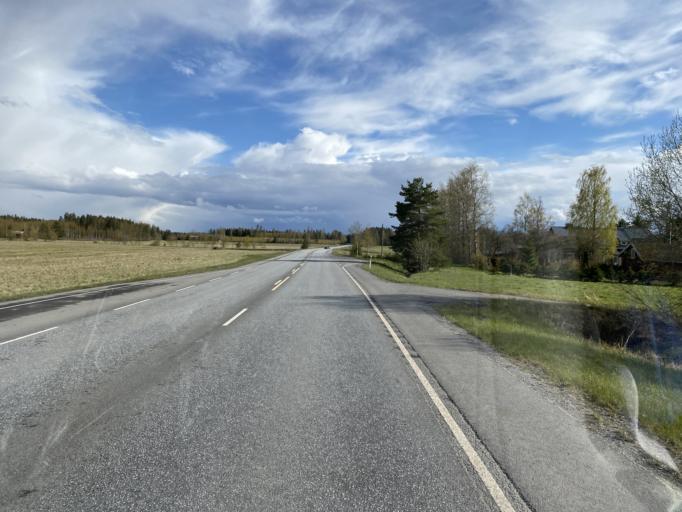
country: FI
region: Pirkanmaa
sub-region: Tampere
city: Lempaeaelae
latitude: 61.2915
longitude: 23.7422
